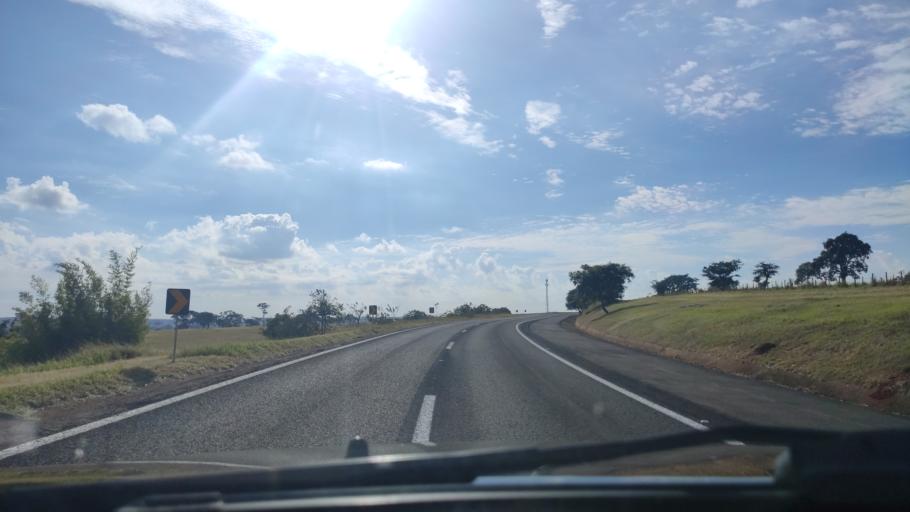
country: BR
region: Sao Paulo
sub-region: Avare
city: Avare
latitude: -22.9669
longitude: -48.8116
